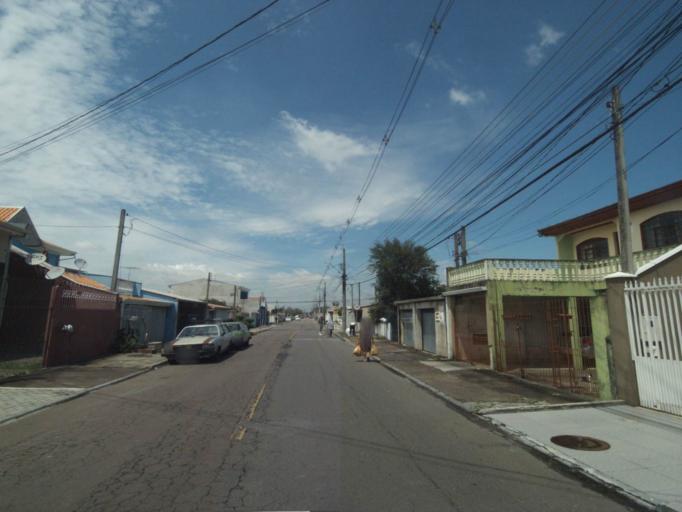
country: BR
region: Parana
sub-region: Pinhais
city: Pinhais
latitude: -25.4690
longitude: -49.1970
